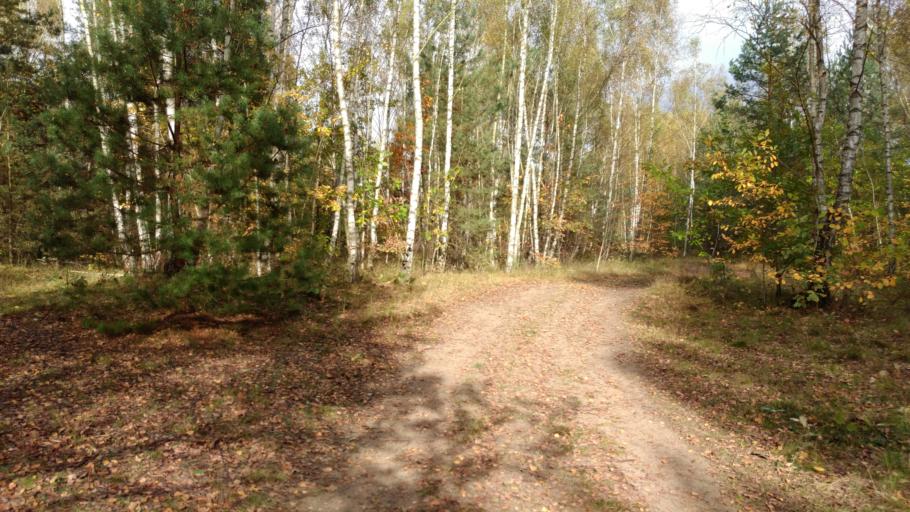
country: DE
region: Saxony
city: Albertstadt
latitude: 51.1024
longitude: 13.7498
